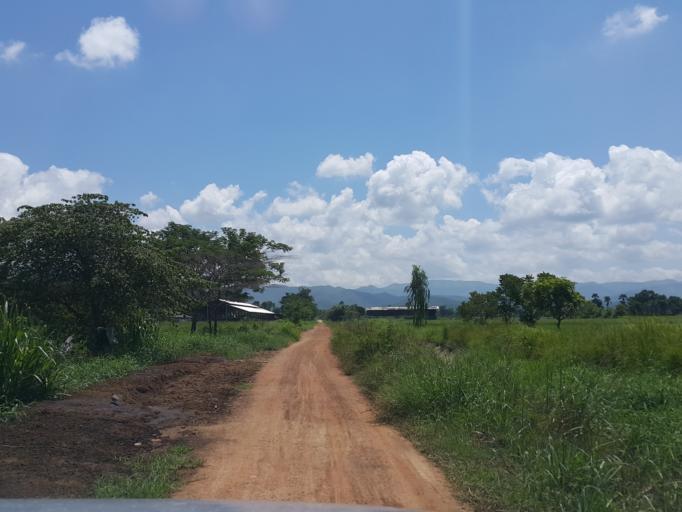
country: TH
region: Lamphun
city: Ban Thi
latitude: 18.6724
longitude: 99.1435
